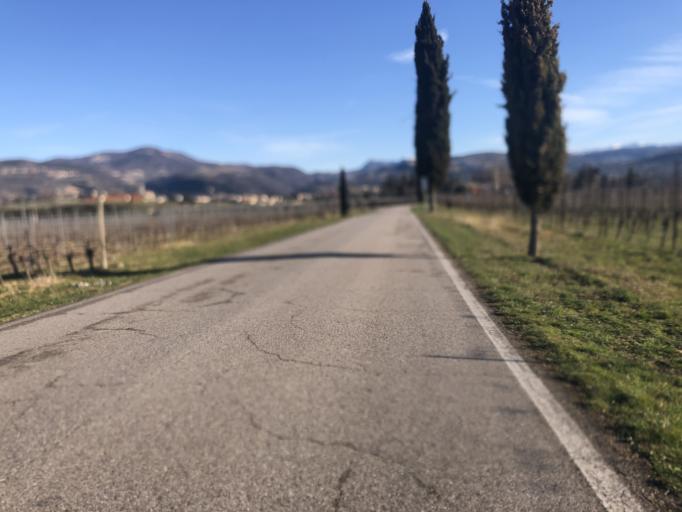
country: IT
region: Veneto
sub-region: Provincia di Verona
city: San Pietro in Cariano
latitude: 45.5018
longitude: 10.8803
